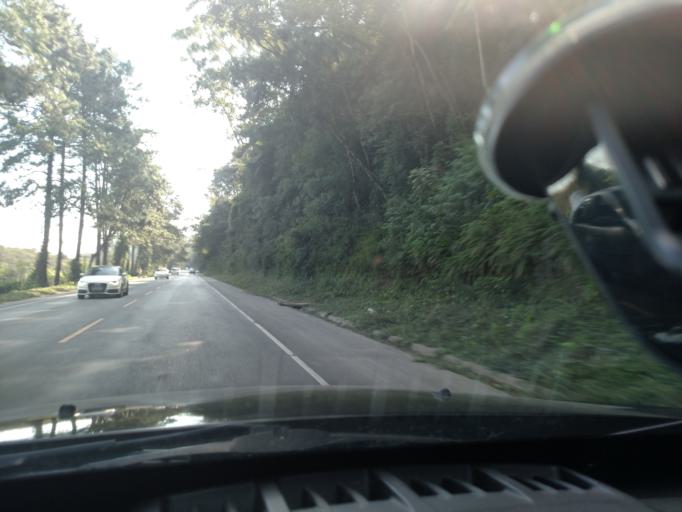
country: BR
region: Santa Catarina
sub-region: Rio Do Sul
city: Rio do Sul
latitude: -27.2337
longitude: -49.6743
